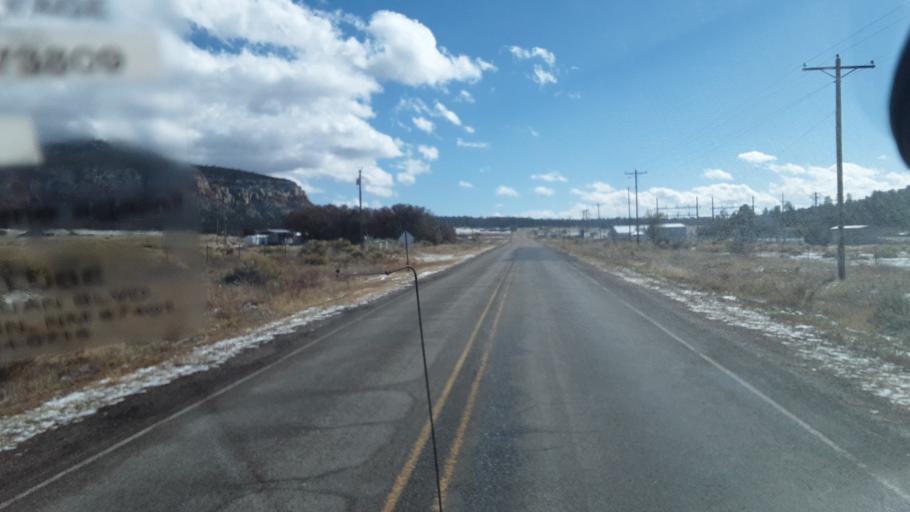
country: US
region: New Mexico
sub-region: Rio Arriba County
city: Santa Teresa
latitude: 36.2235
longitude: -106.7937
